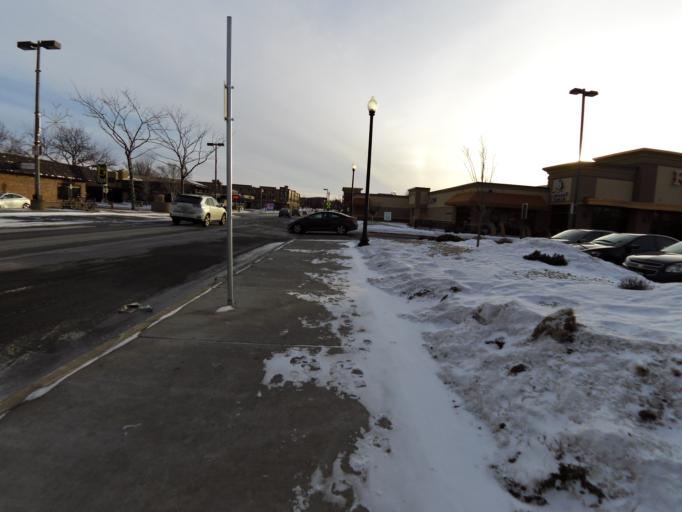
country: US
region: Wisconsin
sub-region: Pierce County
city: River Falls
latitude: 44.8569
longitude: -92.6271
